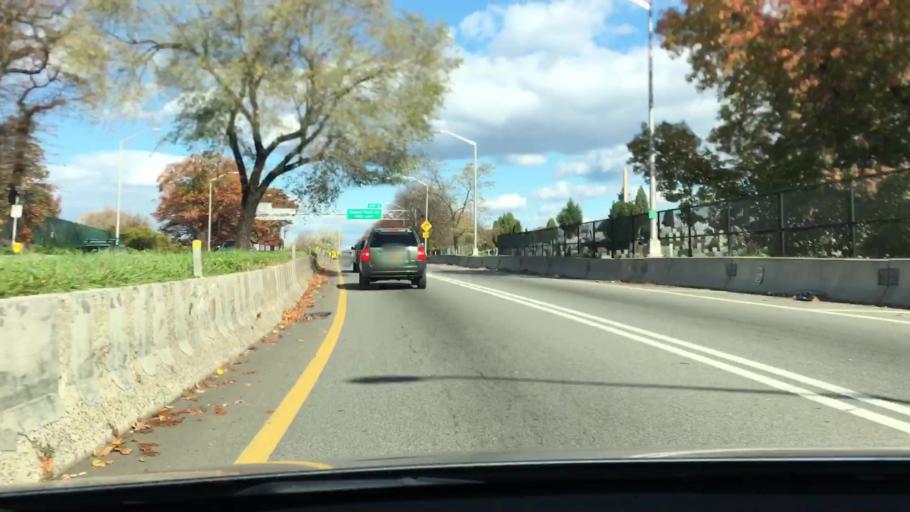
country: US
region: New York
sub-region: Kings County
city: East New York
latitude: 40.6956
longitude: -73.8752
